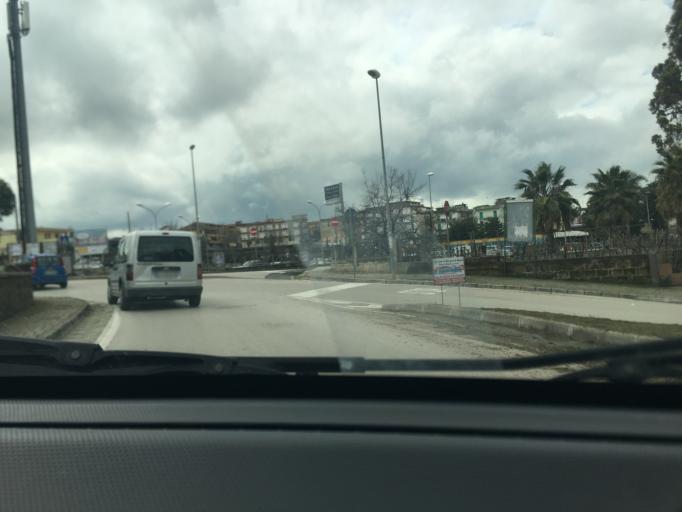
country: IT
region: Campania
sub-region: Provincia di Napoli
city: Calvizzano
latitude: 40.8960
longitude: 14.1983
